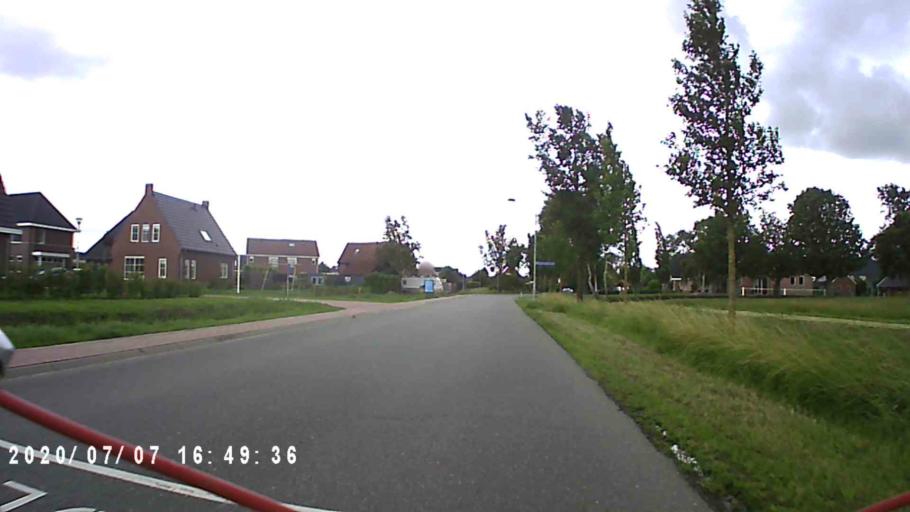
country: NL
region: Groningen
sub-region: Gemeente Winsum
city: Winsum
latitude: 53.3363
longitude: 6.5226
